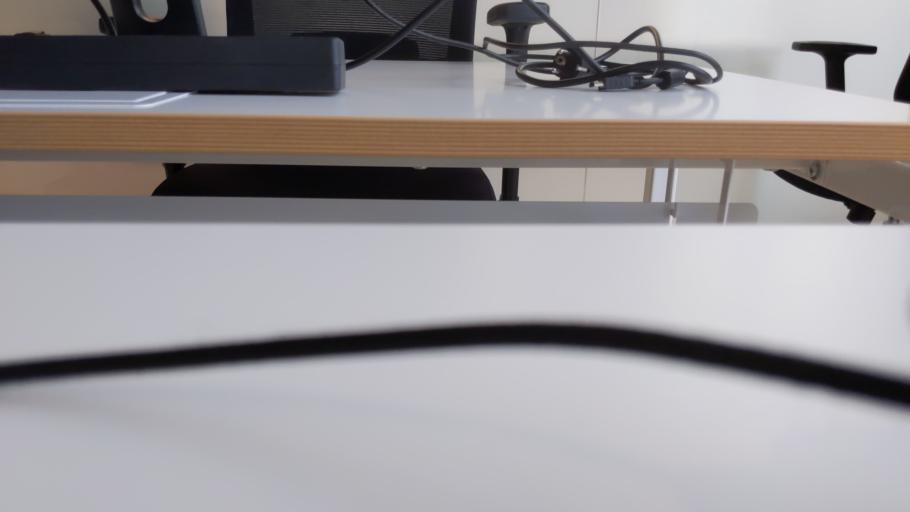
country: RU
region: Moskovskaya
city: Rogachevo
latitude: 56.4104
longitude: 37.0677
